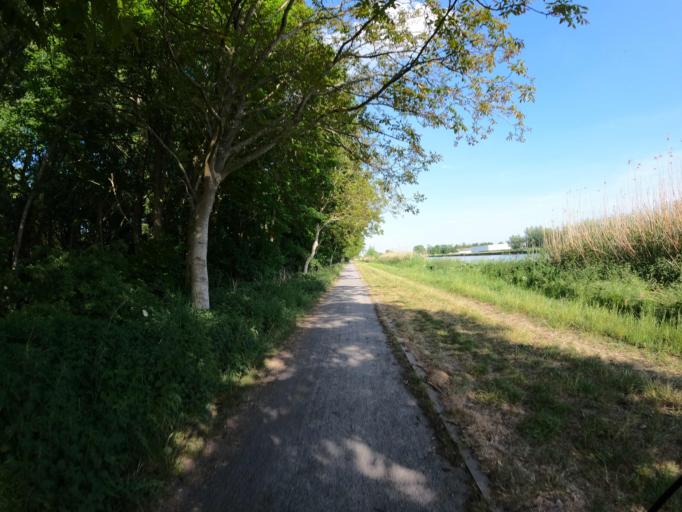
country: BE
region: Flanders
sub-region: Provincie West-Vlaanderen
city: Ingelmunster
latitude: 50.9193
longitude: 3.2381
